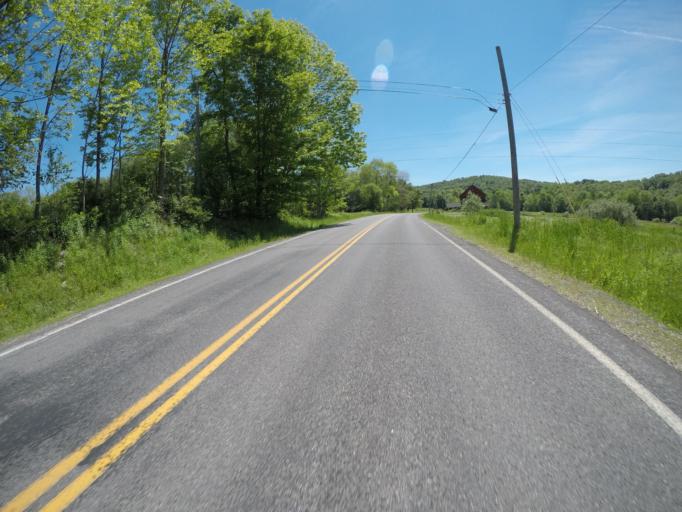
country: US
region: New York
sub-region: Delaware County
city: Delhi
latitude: 42.2091
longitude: -74.8576
